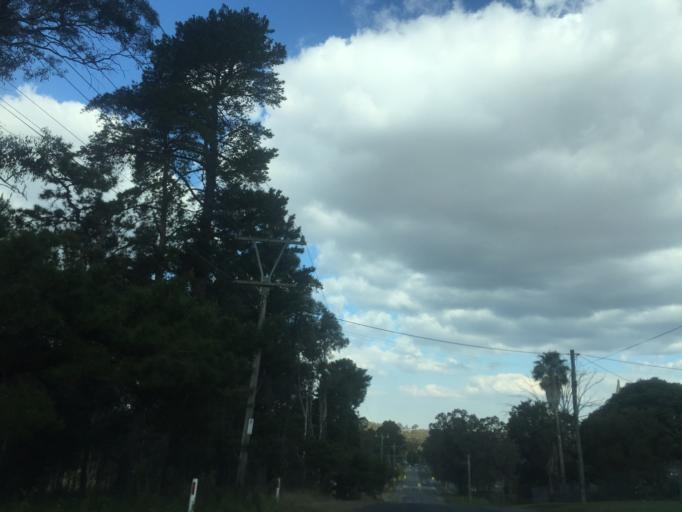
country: AU
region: New South Wales
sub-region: Blacktown
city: Rouse Hill
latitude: -33.6815
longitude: 150.9075
